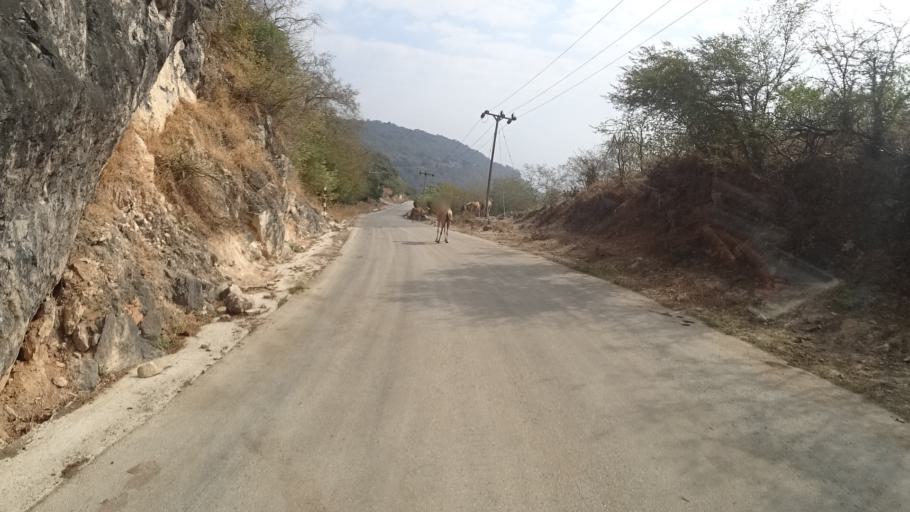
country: YE
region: Al Mahrah
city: Hawf
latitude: 16.7073
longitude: 53.2235
